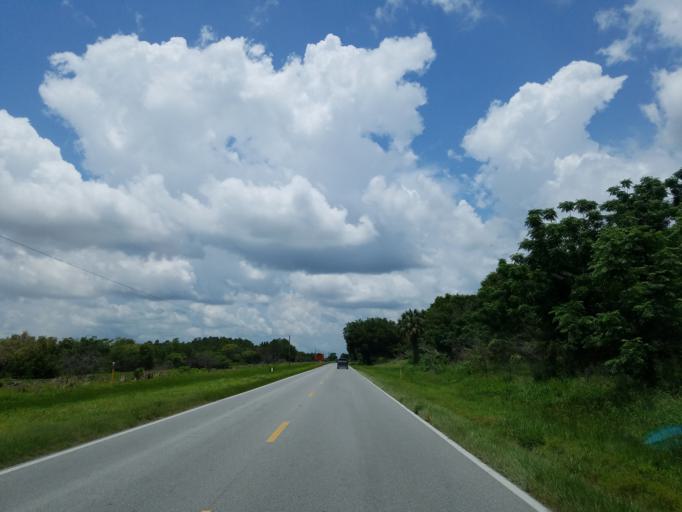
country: US
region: Florida
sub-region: Polk County
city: Mulberry
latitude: 27.8509
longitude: -81.9939
